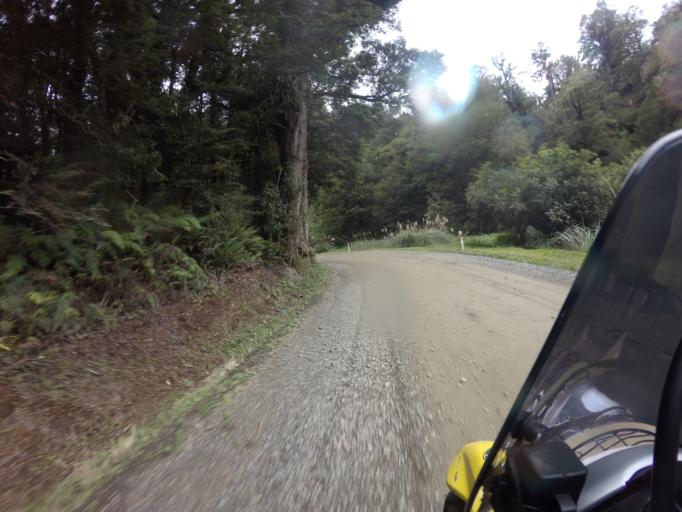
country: NZ
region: Bay of Plenty
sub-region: Whakatane District
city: Murupara
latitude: -38.6757
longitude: 177.0520
